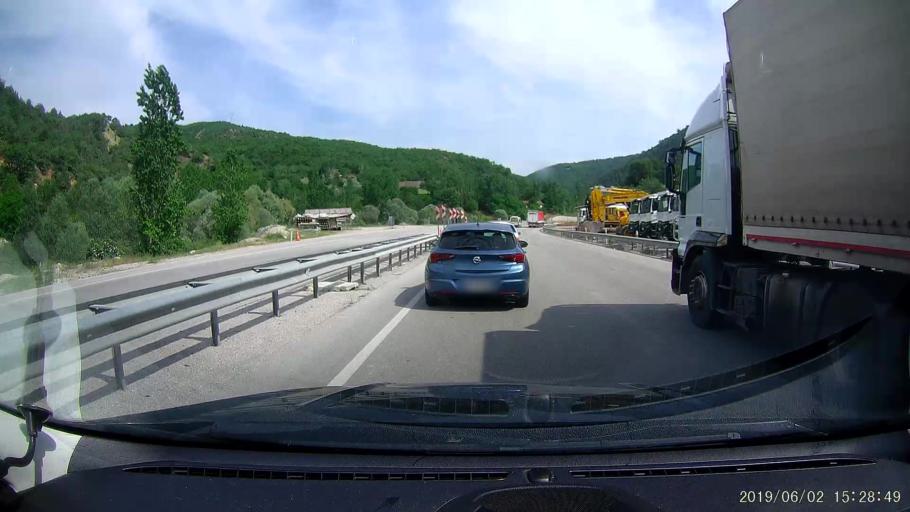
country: TR
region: Amasya
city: Saraycik
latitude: 40.9742
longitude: 35.0817
